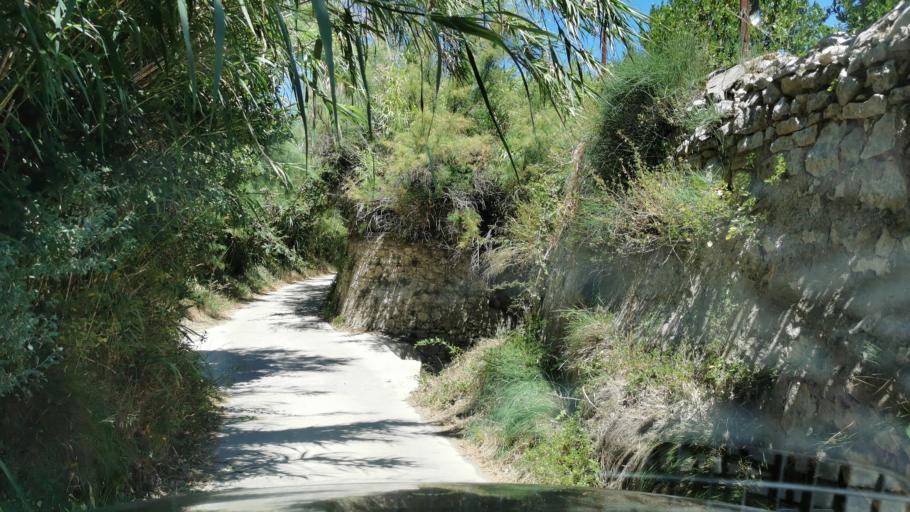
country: FR
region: Languedoc-Roussillon
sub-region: Departement de l'Aude
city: Peyriac-de-Mer
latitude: 43.0932
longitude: 2.9577
